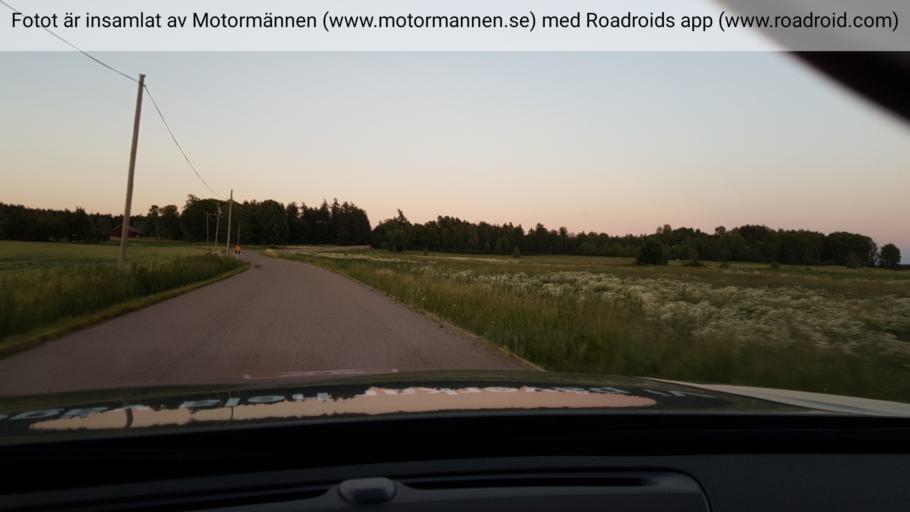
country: SE
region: Vaestmanland
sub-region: Hallstahammars Kommun
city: Kolback
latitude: 59.5253
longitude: 16.1819
